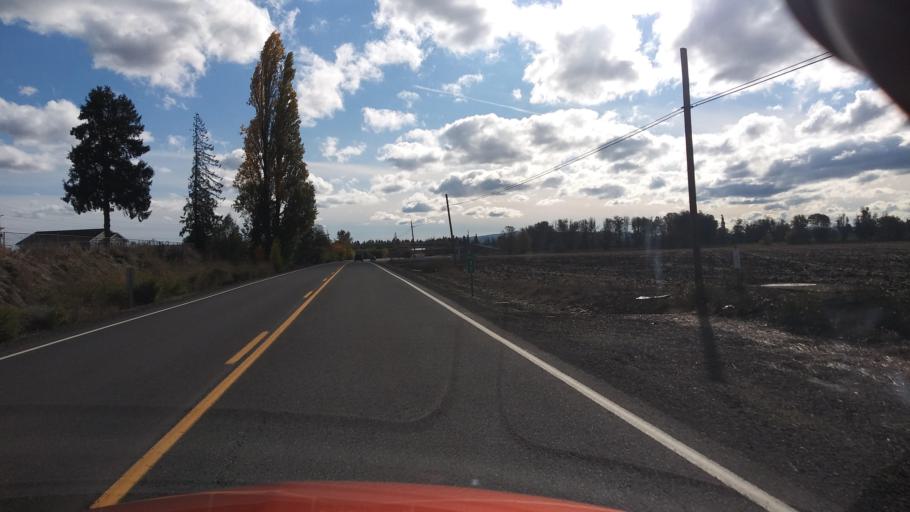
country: US
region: Oregon
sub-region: Washington County
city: Banks
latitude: 45.5778
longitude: -123.1111
